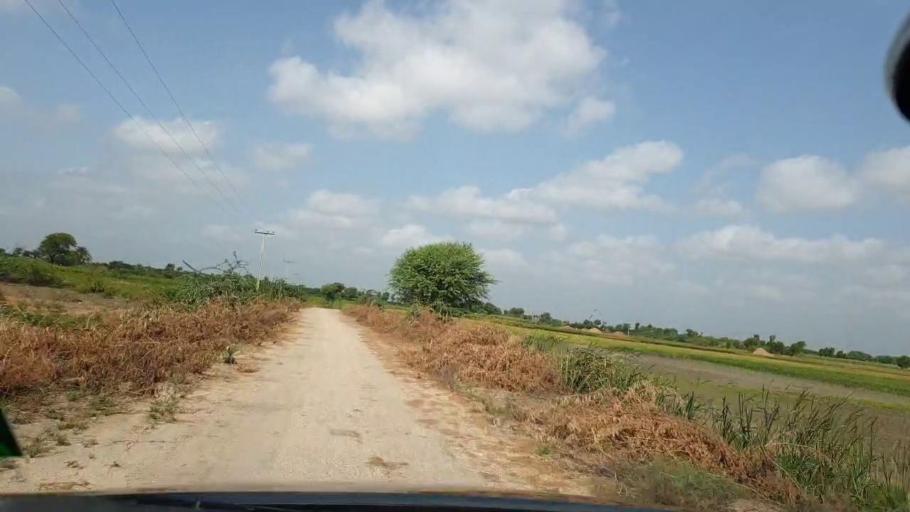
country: PK
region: Sindh
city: Kadhan
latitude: 24.6191
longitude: 69.1068
